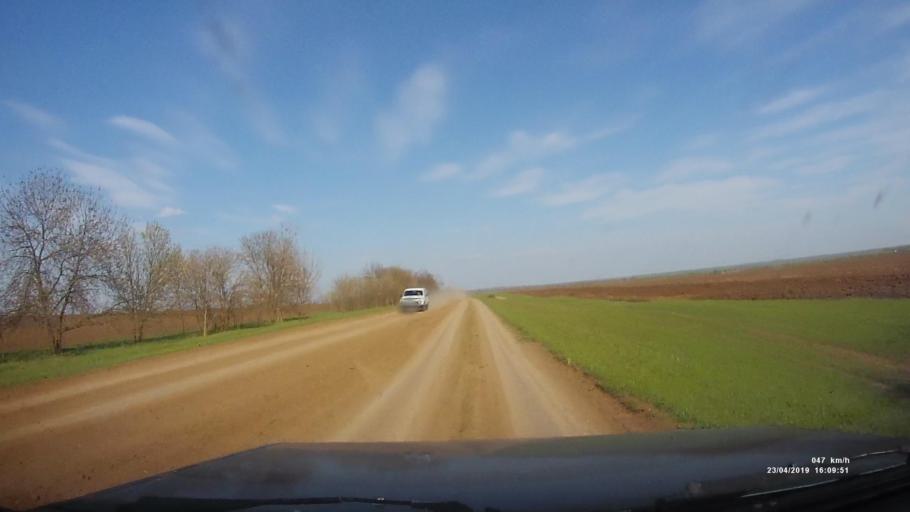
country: RU
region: Rostov
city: Remontnoye
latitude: 46.4815
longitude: 43.1155
